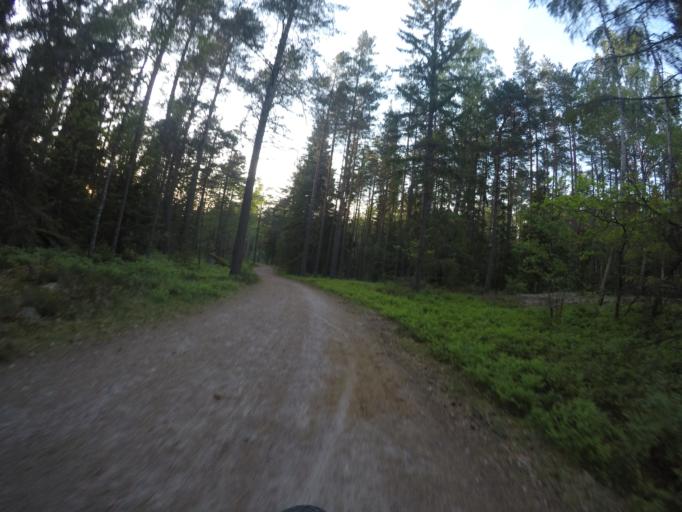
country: SE
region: Soedermanland
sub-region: Eskilstuna Kommun
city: Eskilstuna
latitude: 59.3424
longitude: 16.5125
